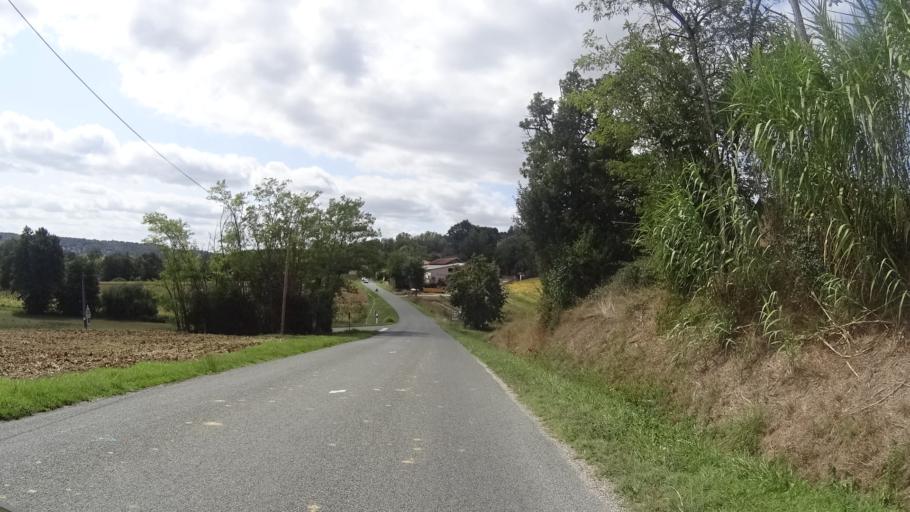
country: FR
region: Aquitaine
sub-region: Departement du Lot-et-Garonne
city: Pont-du-Casse
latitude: 44.2490
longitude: 0.6822
